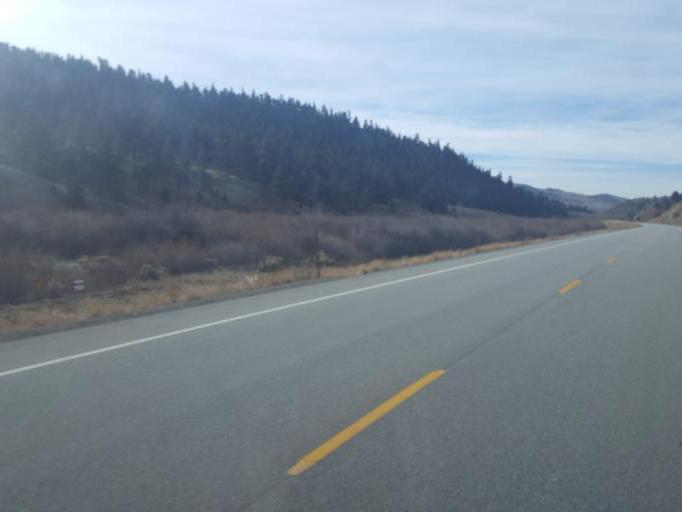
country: US
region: Colorado
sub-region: Costilla County
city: San Luis
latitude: 37.5389
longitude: -105.2902
